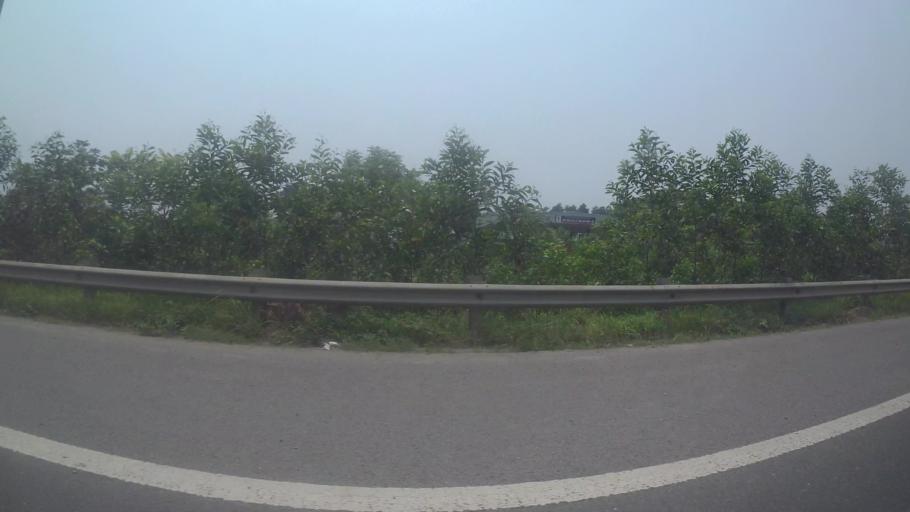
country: VN
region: Ha Noi
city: Quoc Oai
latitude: 20.9907
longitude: 105.5811
